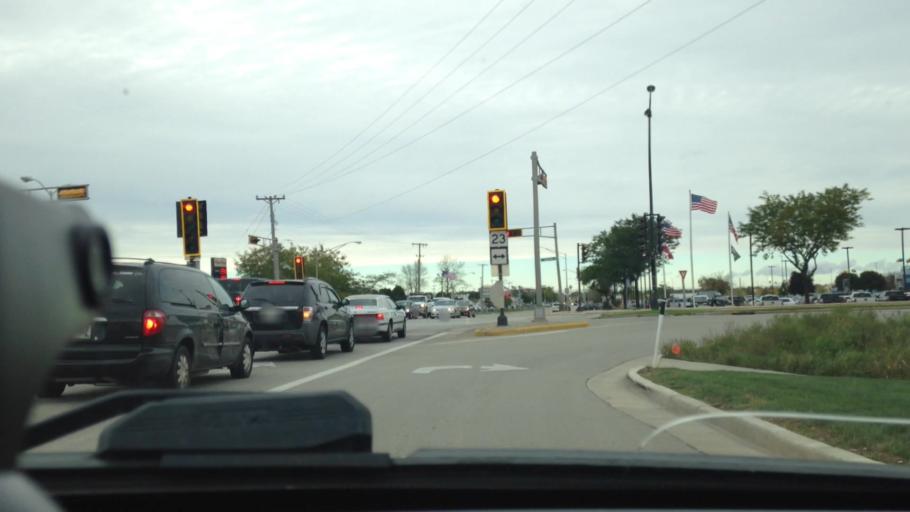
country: US
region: Wisconsin
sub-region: Fond du Lac County
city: North Fond du Lac
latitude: 43.7841
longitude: -88.4858
